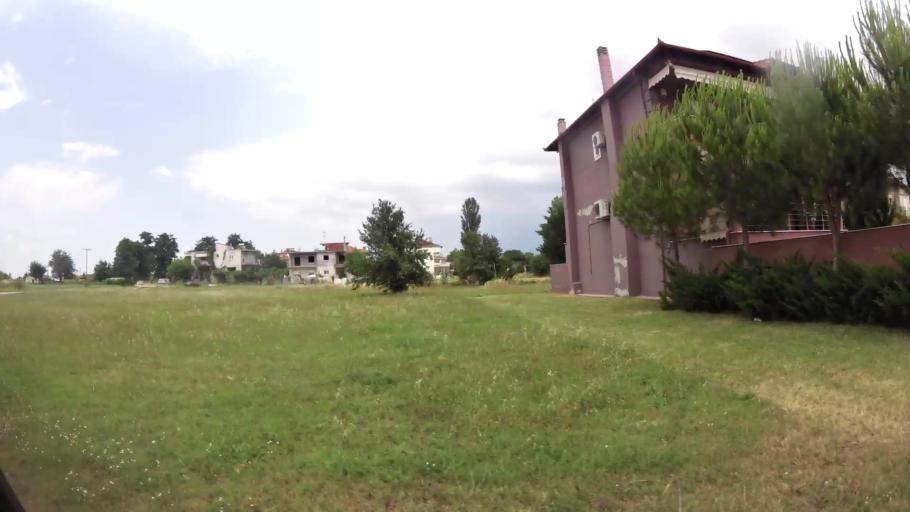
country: GR
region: Central Macedonia
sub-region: Nomos Pierias
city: Kallithea
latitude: 40.2740
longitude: 22.5704
